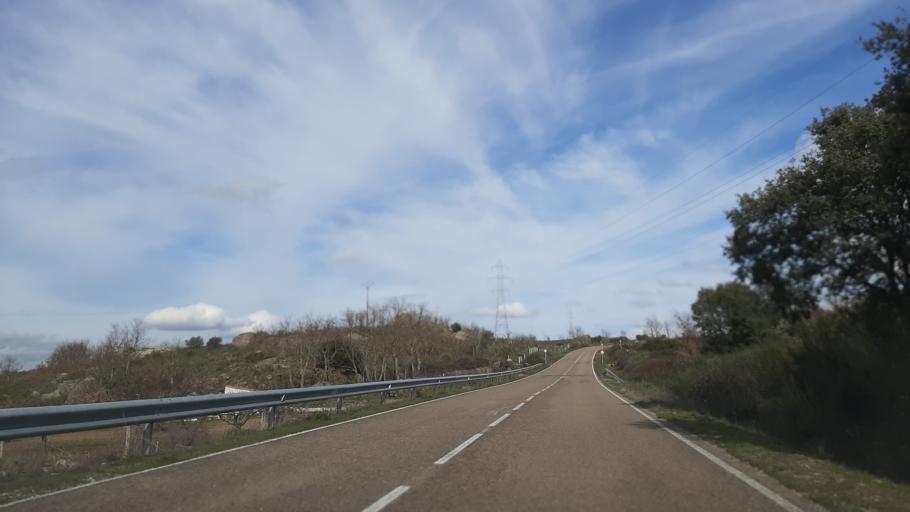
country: ES
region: Castille and Leon
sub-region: Provincia de Salamanca
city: Villarino de los Aires
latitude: 41.2415
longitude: -6.5111
